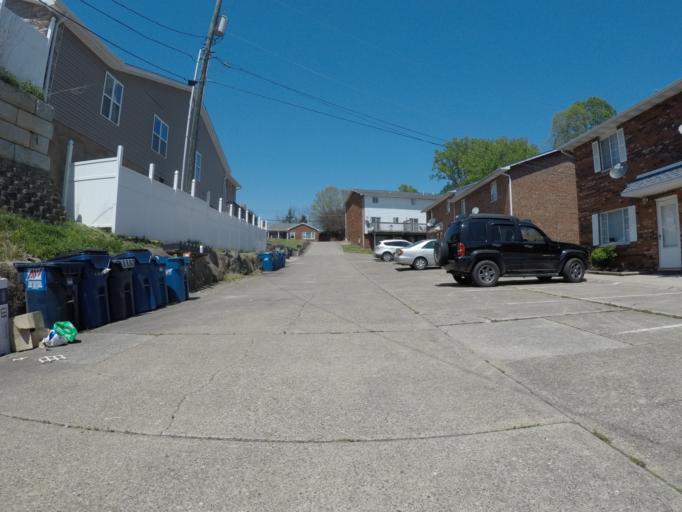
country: US
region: West Virginia
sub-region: Cabell County
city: Pea Ridge
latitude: 38.4089
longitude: -82.3415
